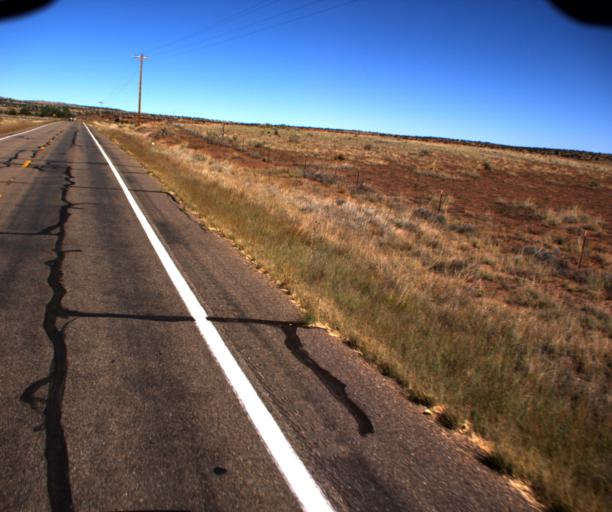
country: US
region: Arizona
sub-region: Apache County
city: Saint Johns
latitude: 34.4398
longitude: -109.4106
